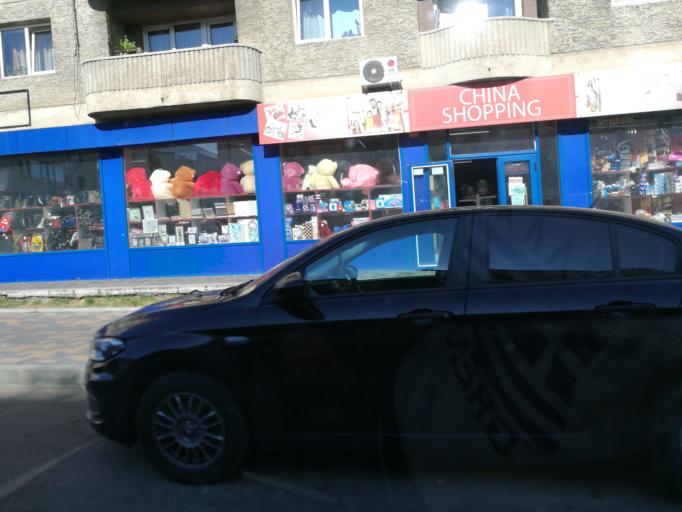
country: RO
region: Suceava
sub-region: Municipiul Falticeni
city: Falticeni
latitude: 47.4551
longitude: 26.2970
